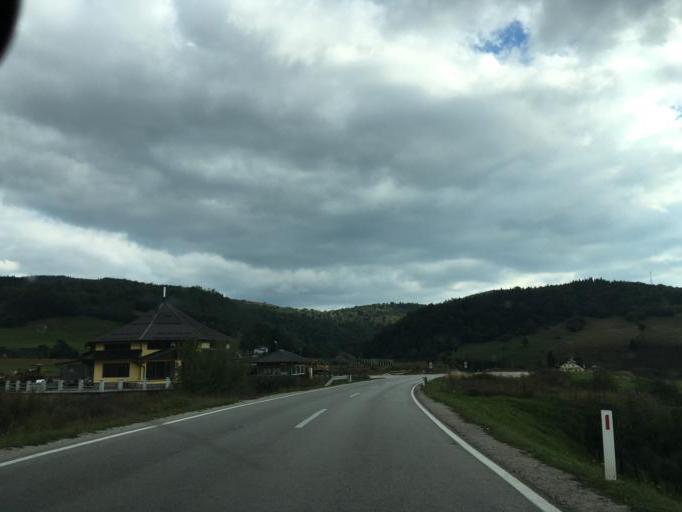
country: BA
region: Federation of Bosnia and Herzegovina
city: Novi Travnik
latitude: 44.1040
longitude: 17.5752
